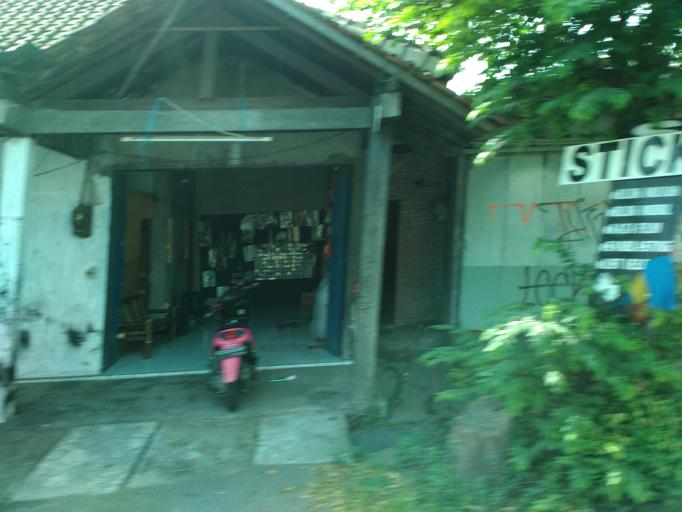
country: ID
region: Central Java
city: Jogonalan
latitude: -7.7321
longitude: 110.5446
